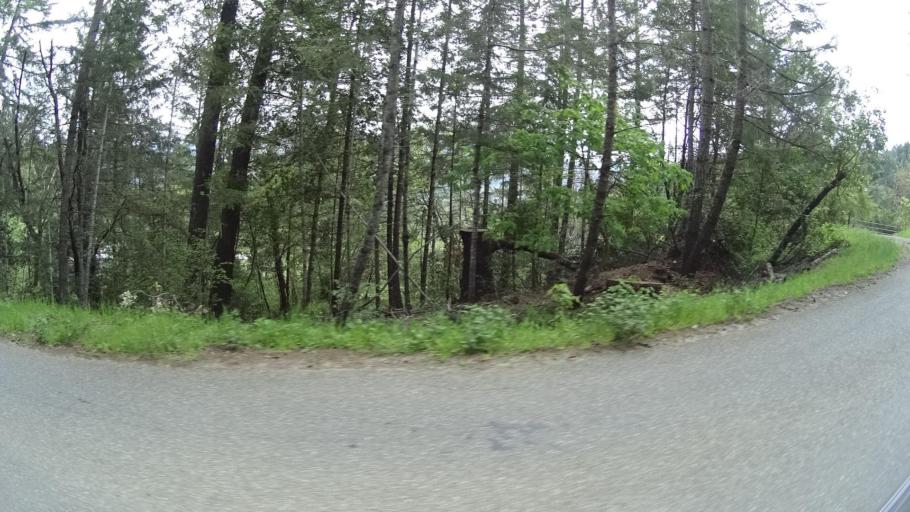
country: US
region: California
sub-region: Humboldt County
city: Redway
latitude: 40.1415
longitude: -123.6294
